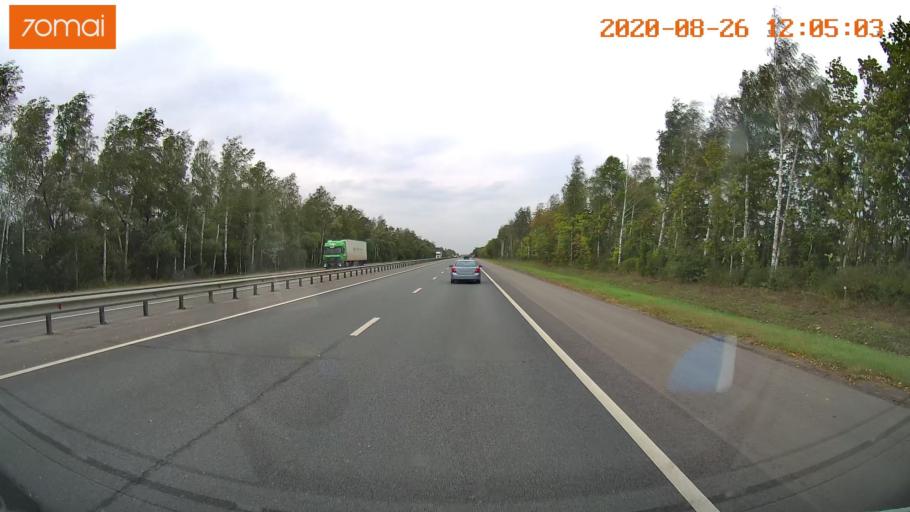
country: RU
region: Rjazan
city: Kiritsy
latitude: 54.3167
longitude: 40.1762
